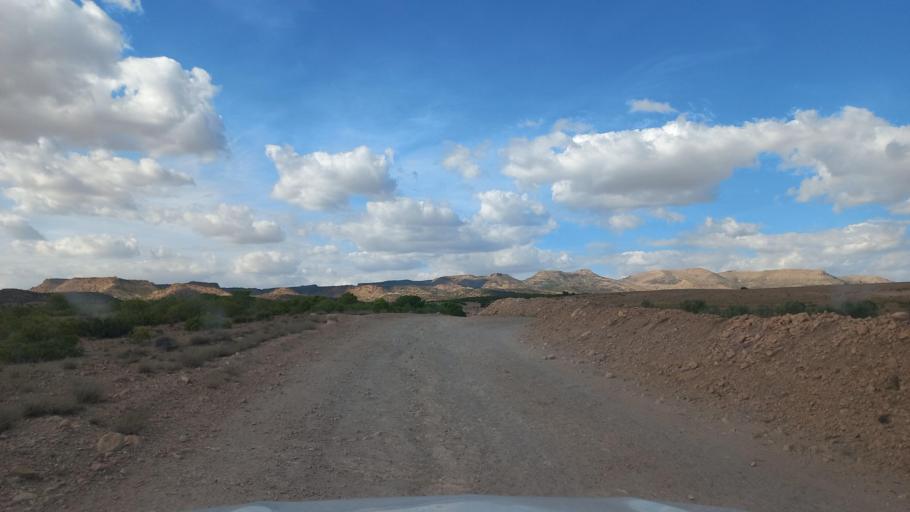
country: TN
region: Al Qasrayn
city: Sbiba
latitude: 35.3998
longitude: 9.0111
